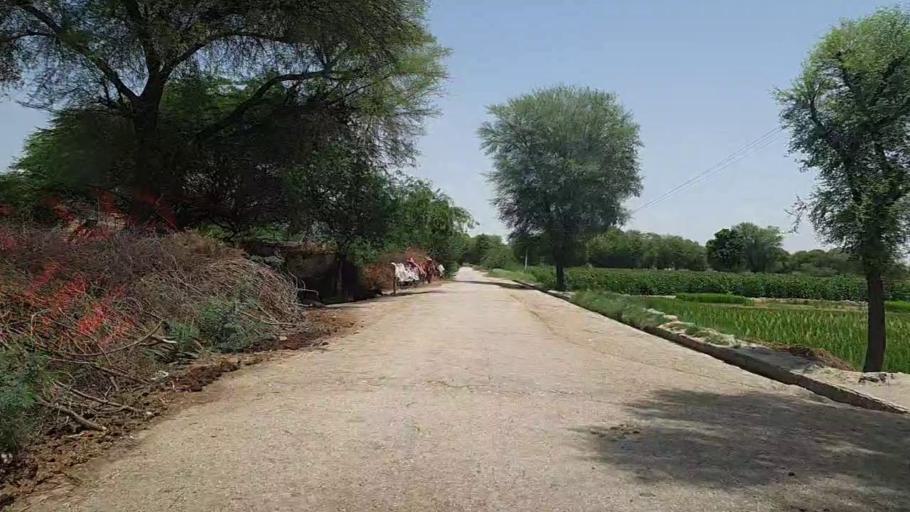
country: PK
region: Sindh
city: Pad Idan
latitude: 26.7444
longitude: 68.3077
